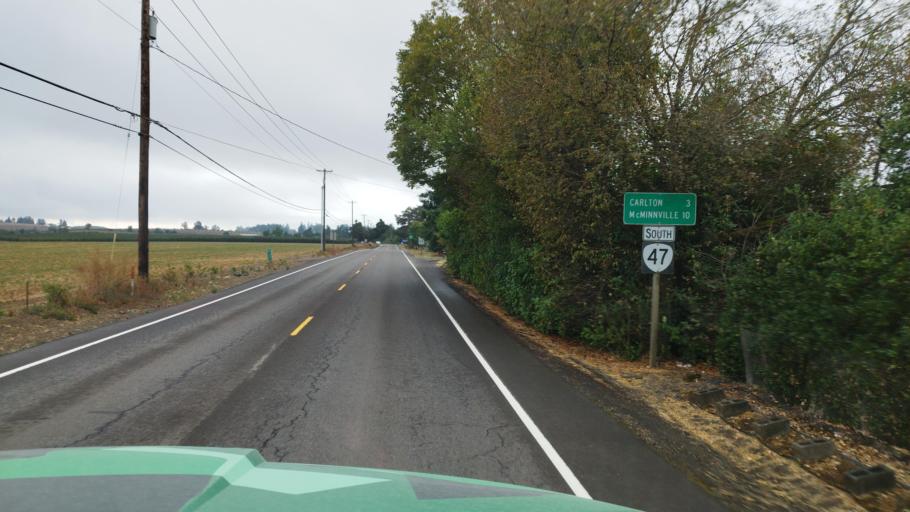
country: US
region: Oregon
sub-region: Yamhill County
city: Yamhill
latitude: 45.3350
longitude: -123.1857
